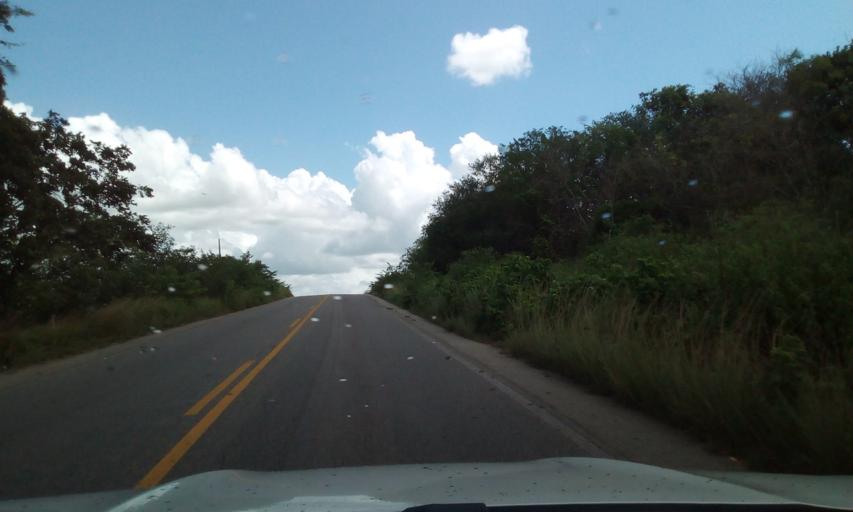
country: BR
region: Paraiba
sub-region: Guarabira
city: Guarabira
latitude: -6.8485
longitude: -35.3654
